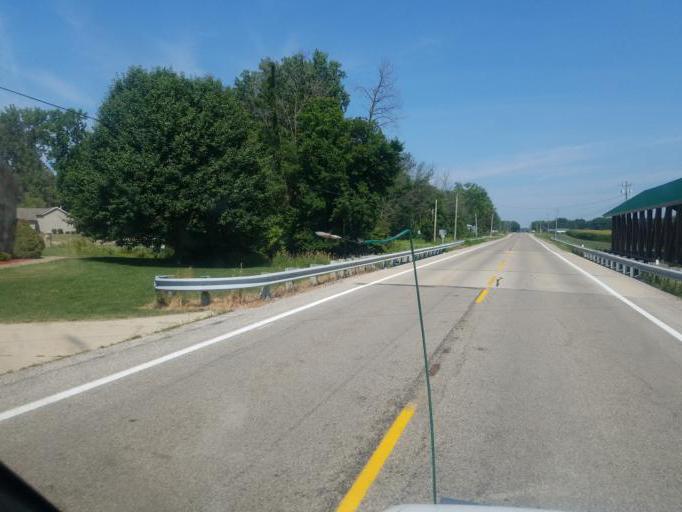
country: US
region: Ohio
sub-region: Mercer County
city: Celina
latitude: 40.5020
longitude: -84.5203
